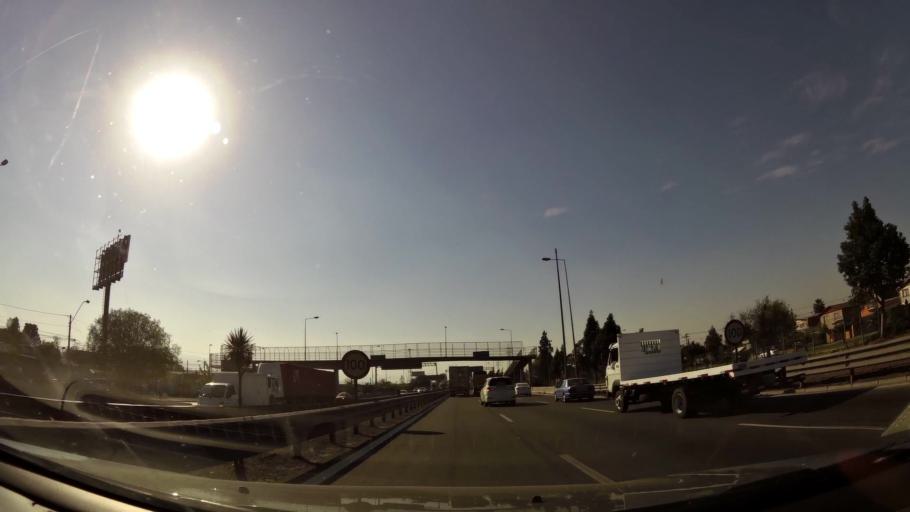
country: CL
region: Santiago Metropolitan
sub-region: Provincia de Santiago
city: Lo Prado
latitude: -33.4948
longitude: -70.7467
